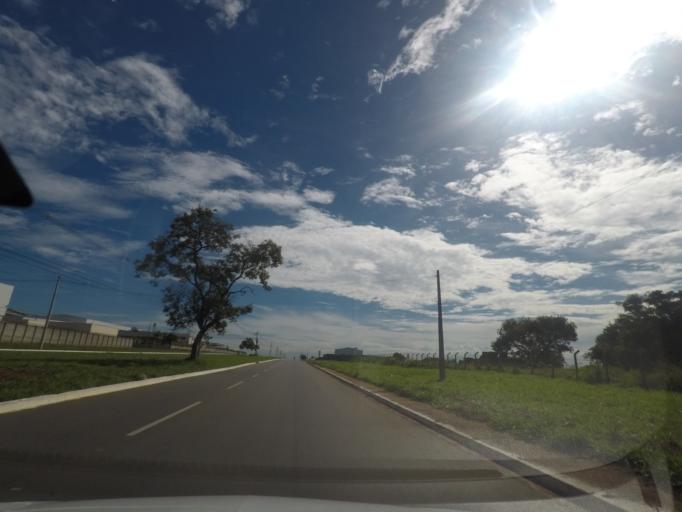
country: BR
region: Goias
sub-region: Aparecida De Goiania
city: Aparecida de Goiania
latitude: -16.8065
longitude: -49.2639
